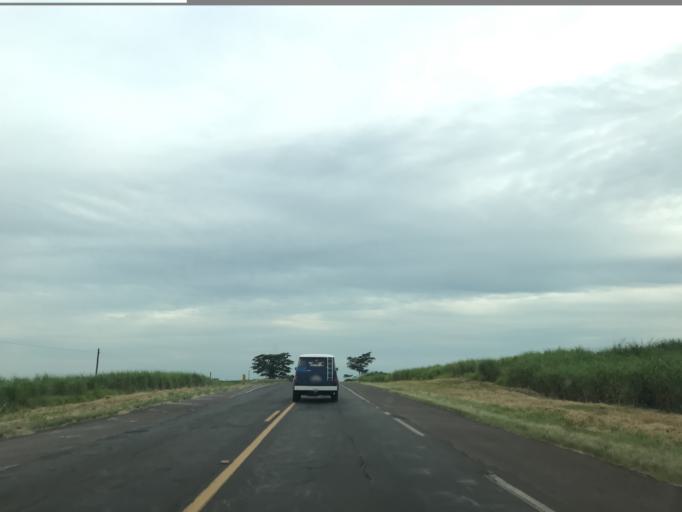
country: BR
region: Sao Paulo
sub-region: Tupa
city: Tupa
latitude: -21.6258
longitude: -50.4864
